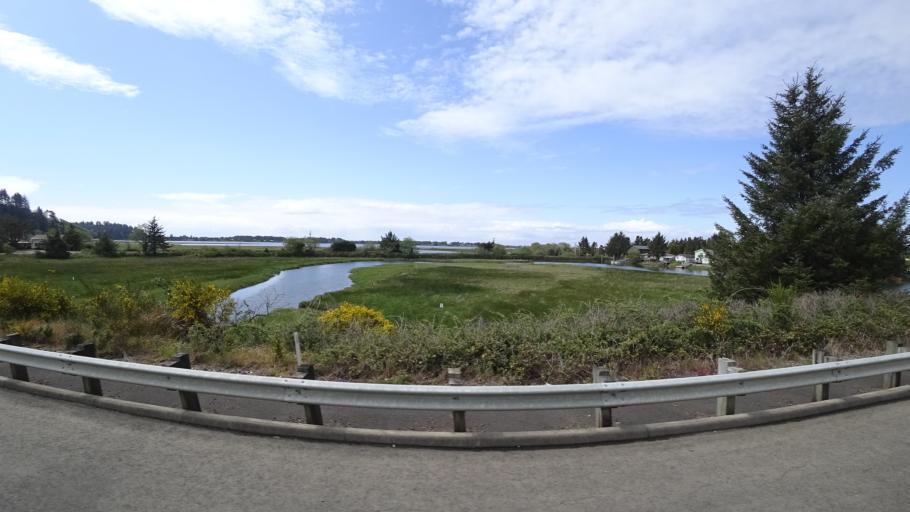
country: US
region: Oregon
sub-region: Lincoln County
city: Lincoln Beach
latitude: 44.8969
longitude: -124.0086
